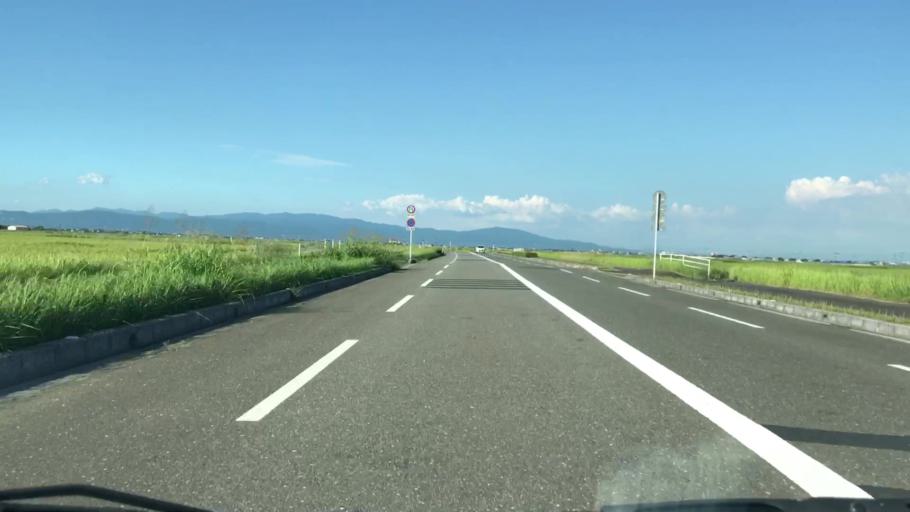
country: JP
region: Saga Prefecture
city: Okawa
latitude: 33.1650
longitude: 130.2919
